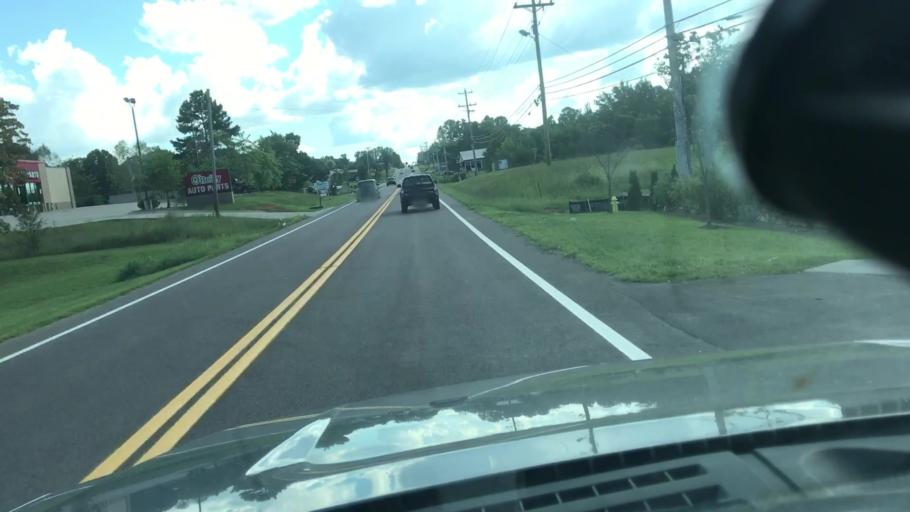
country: US
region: Tennessee
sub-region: Williamson County
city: Fairview
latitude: 35.9652
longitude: -87.1337
